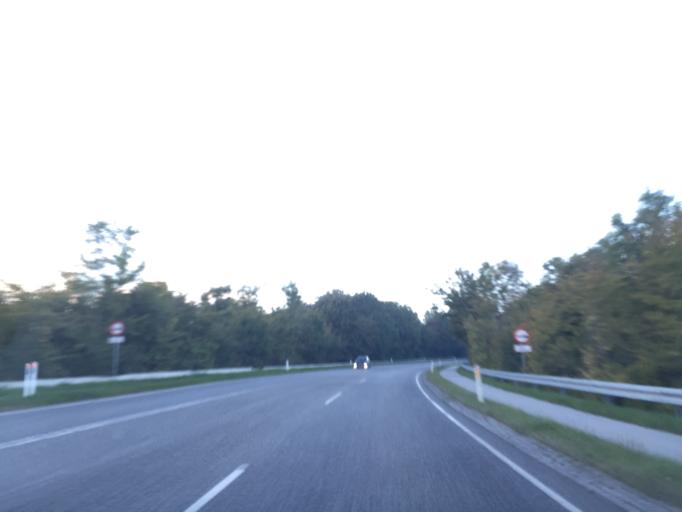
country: DK
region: South Denmark
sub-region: Aabenraa Kommune
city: Aabenraa
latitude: 55.0651
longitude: 9.4316
